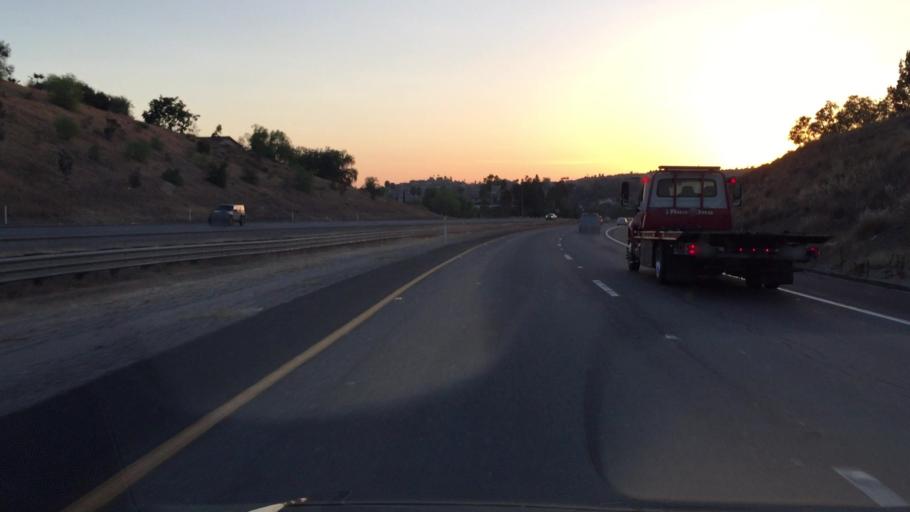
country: US
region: California
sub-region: San Diego County
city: Spring Valley
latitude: 32.7448
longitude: -116.9836
